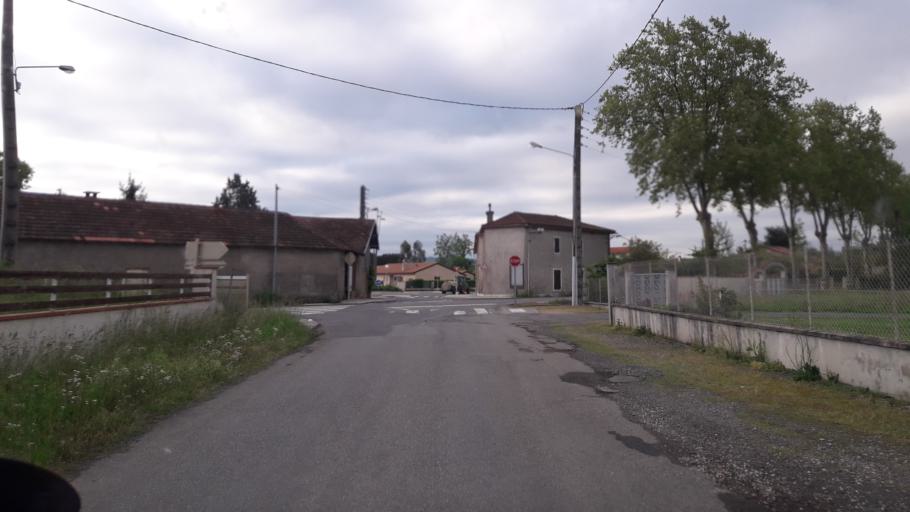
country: FR
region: Midi-Pyrenees
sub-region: Departement de la Haute-Garonne
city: Cazeres
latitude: 43.2183
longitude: 1.0848
